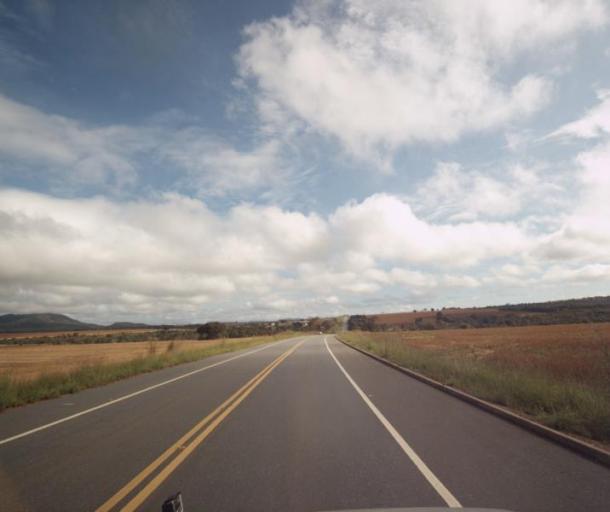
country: BR
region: Goias
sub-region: Barro Alto
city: Barro Alto
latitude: -15.2682
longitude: -48.6859
